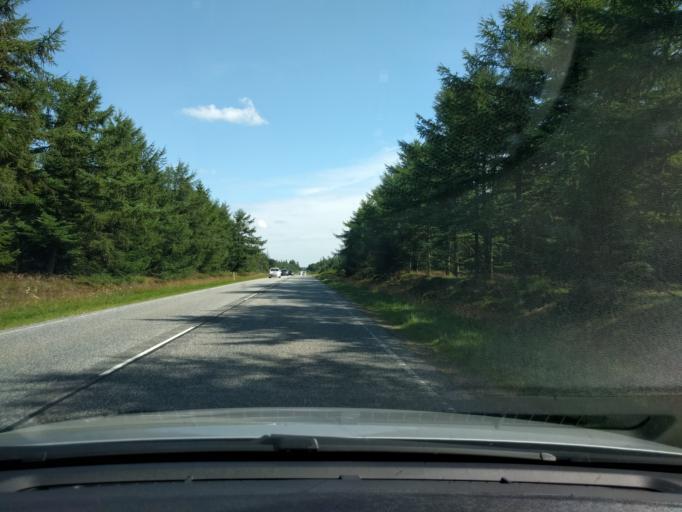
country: DK
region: Central Jutland
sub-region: Herning Kommune
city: Kibaek
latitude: 56.0583
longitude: 8.8928
